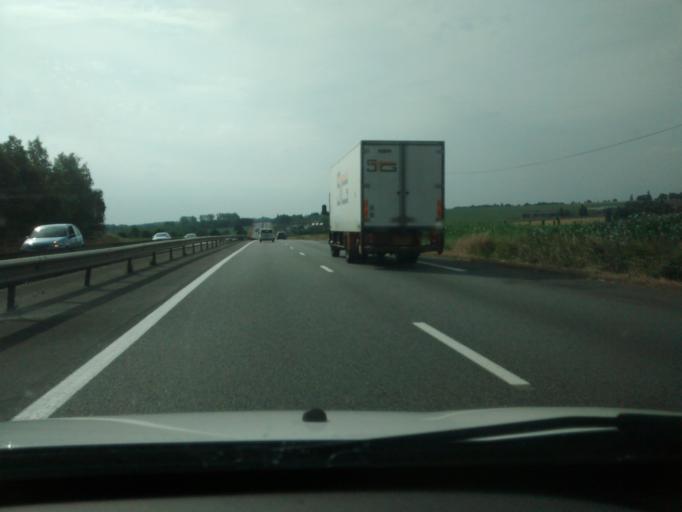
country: FR
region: Brittany
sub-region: Departement d'Ille-et-Vilaine
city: Saint-Gilles
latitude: 48.1623
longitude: -1.8576
